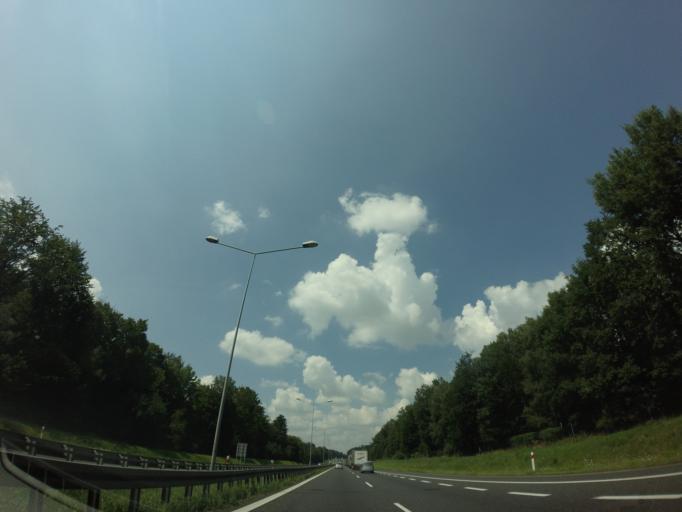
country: PL
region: Opole Voivodeship
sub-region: Powiat strzelecki
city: Ujazd
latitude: 50.4271
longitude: 18.3850
